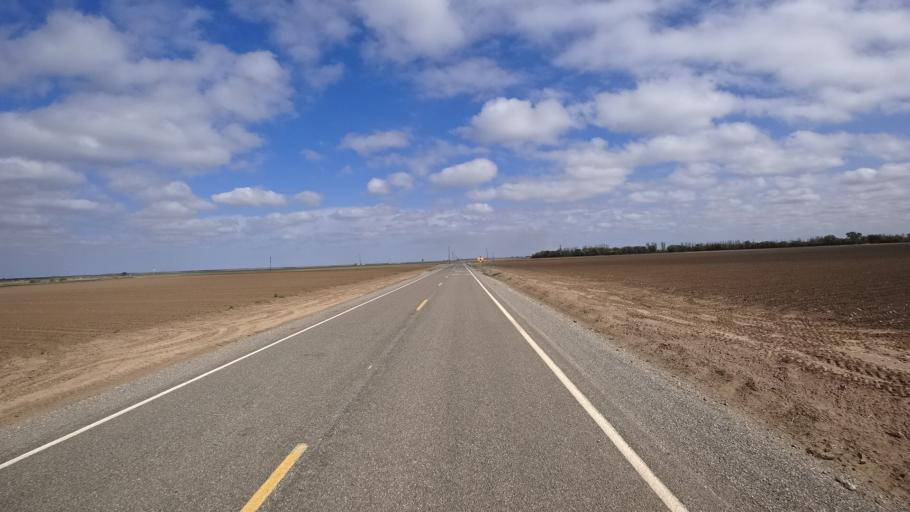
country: US
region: California
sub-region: Butte County
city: Biggs
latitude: 39.4176
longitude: -121.9295
